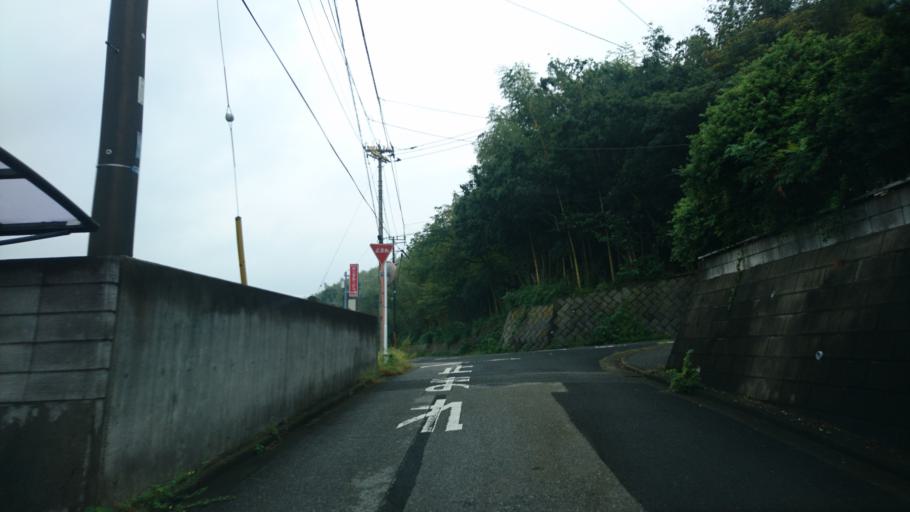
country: JP
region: Chiba
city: Kimitsu
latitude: 35.3322
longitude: 139.9247
